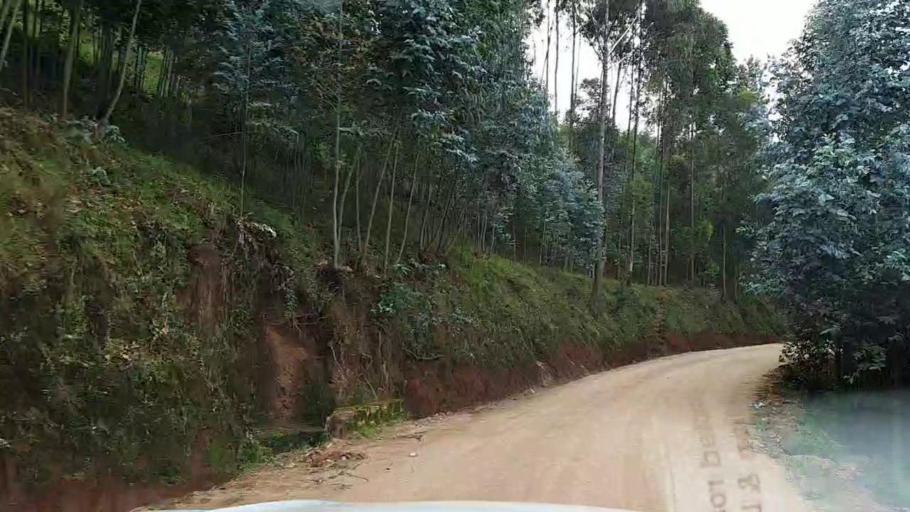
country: RW
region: Southern Province
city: Nzega
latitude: -2.4003
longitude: 29.4543
